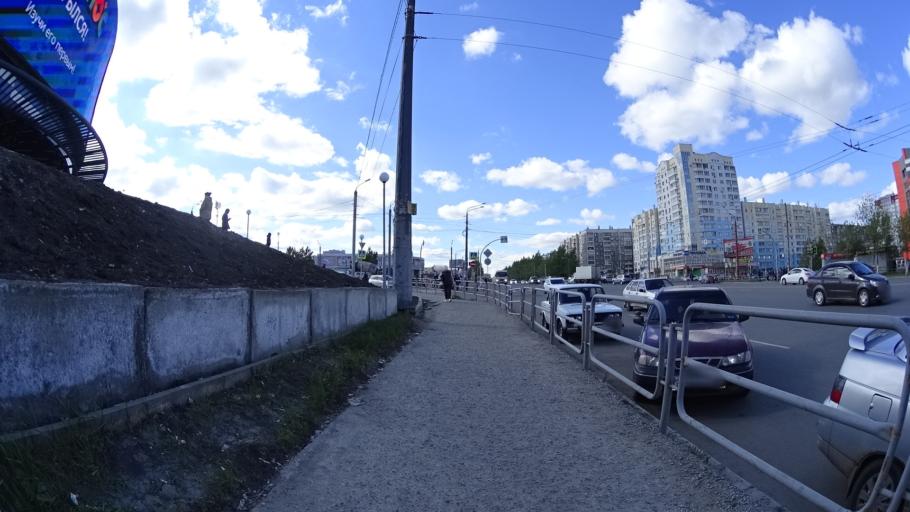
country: RU
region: Chelyabinsk
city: Roshchino
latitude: 55.1819
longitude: 61.2928
